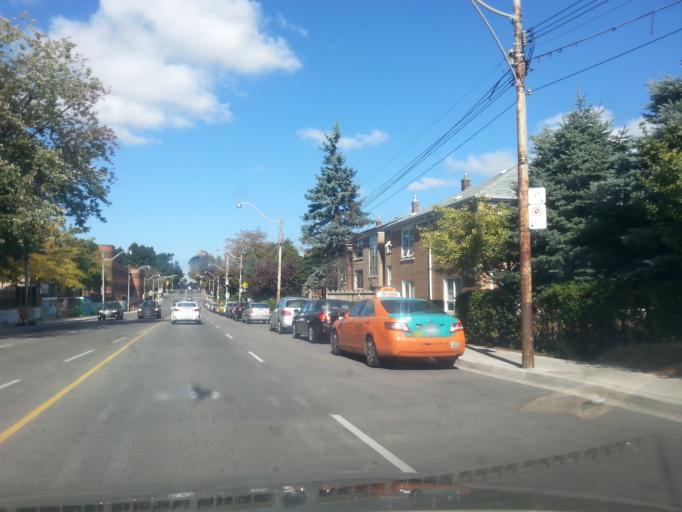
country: CA
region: Ontario
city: Toronto
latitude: 43.6563
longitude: -79.4605
